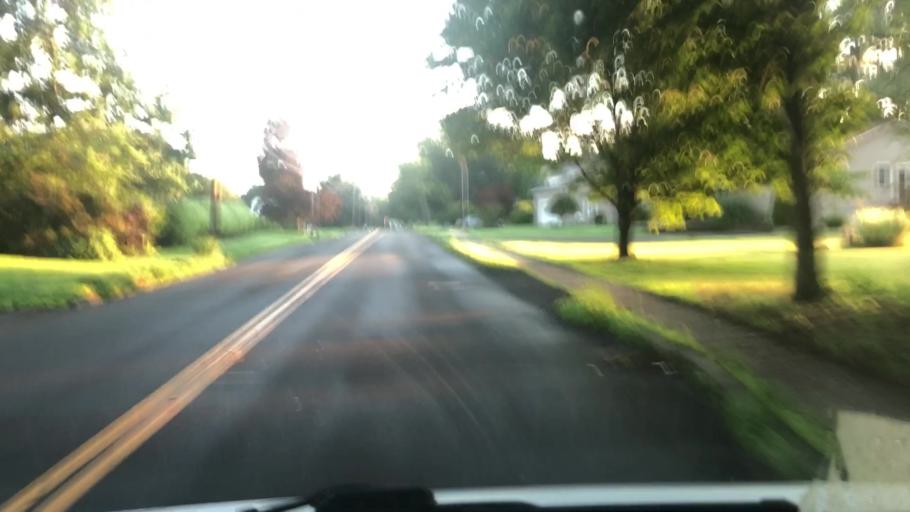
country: US
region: Massachusetts
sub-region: Hampshire County
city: Easthampton
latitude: 42.2718
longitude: -72.6674
